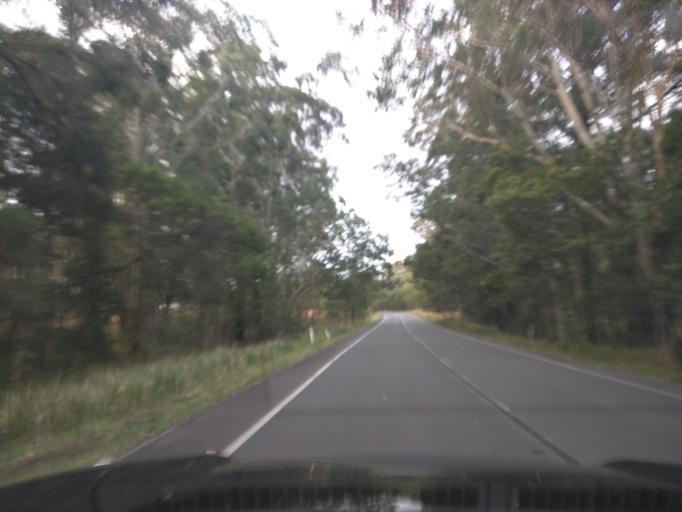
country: AU
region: New South Wales
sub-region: Wollondilly
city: Douglas Park
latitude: -34.2648
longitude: 150.7173
